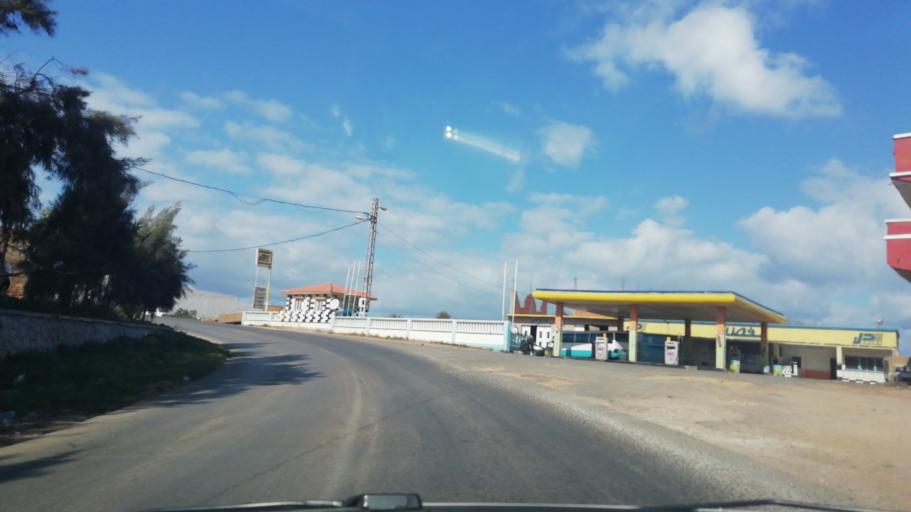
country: DZ
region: Relizane
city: Mazouna
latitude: 36.3235
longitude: 0.6781
